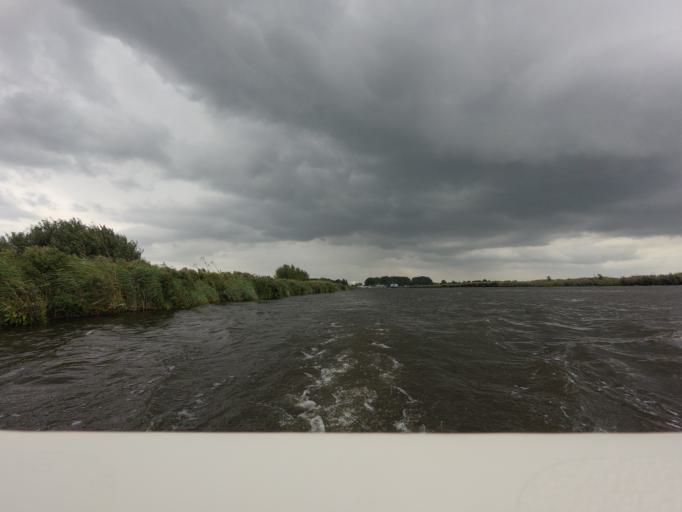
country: NL
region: Friesland
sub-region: Gemeente Smallingerland
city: Oudega
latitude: 53.1107
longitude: 5.9477
